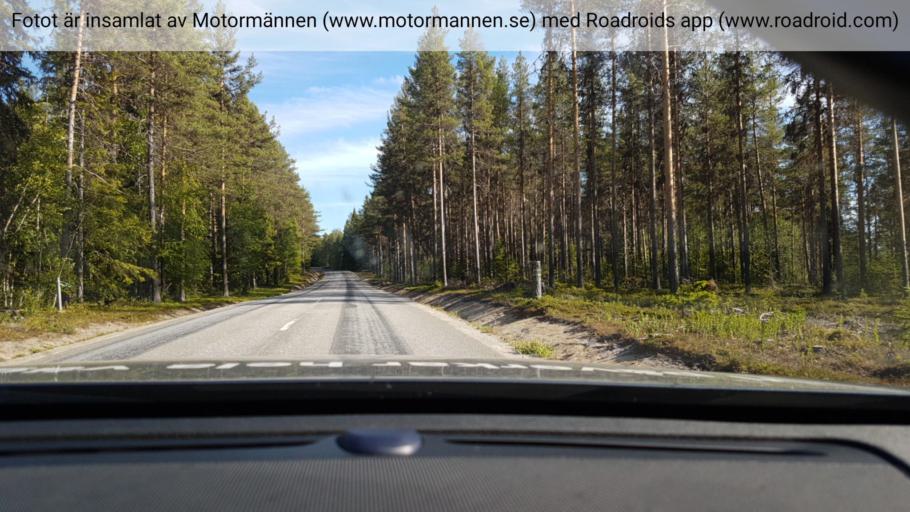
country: SE
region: Vaesterbotten
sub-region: Norsjo Kommun
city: Norsjoe
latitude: 64.6503
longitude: 19.2775
